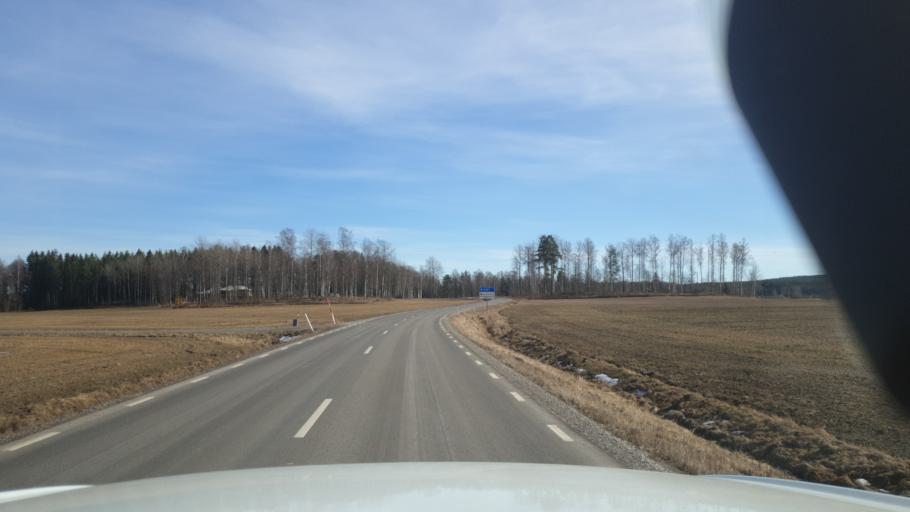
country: SE
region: Vaermland
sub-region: Arvika Kommun
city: Arvika
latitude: 59.5323
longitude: 12.6040
